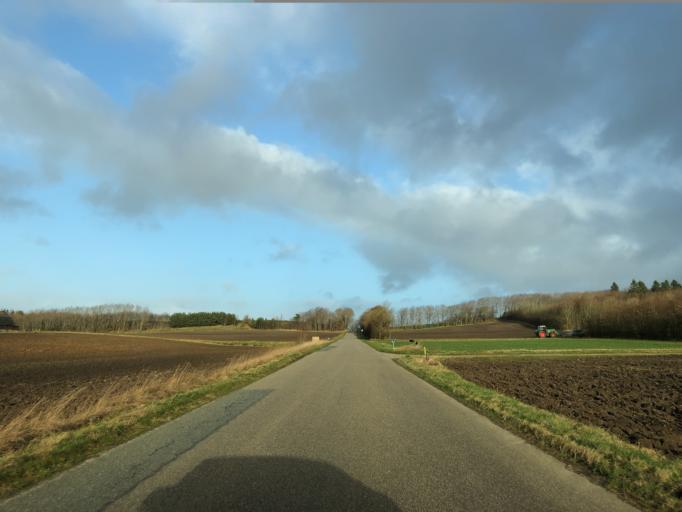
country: DK
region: Central Jutland
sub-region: Ringkobing-Skjern Kommune
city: Videbaek
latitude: 56.1858
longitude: 8.5423
